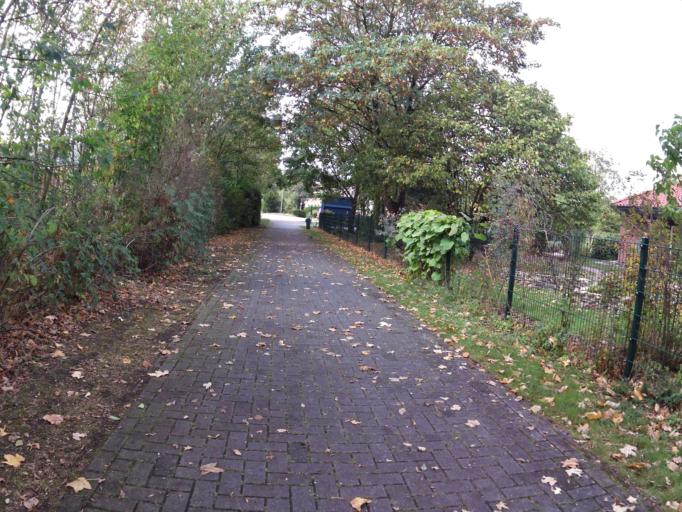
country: DE
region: Lower Saxony
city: Bucken
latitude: 52.7812
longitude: 9.1371
